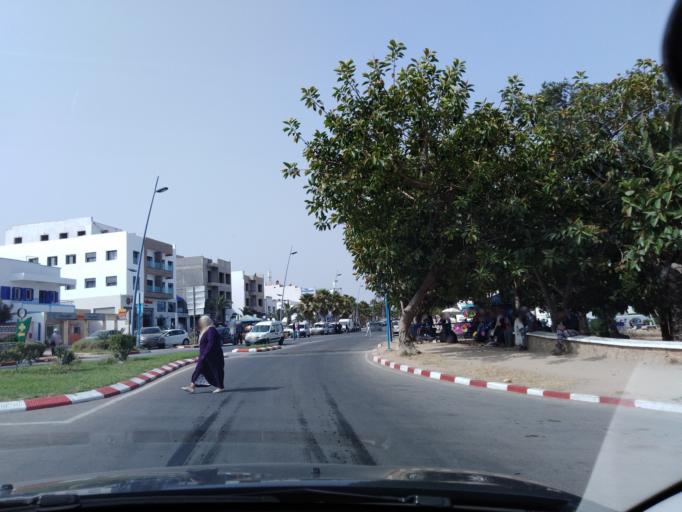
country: MA
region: Doukkala-Abda
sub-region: Safi
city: Safi
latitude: 32.7343
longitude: -9.0336
